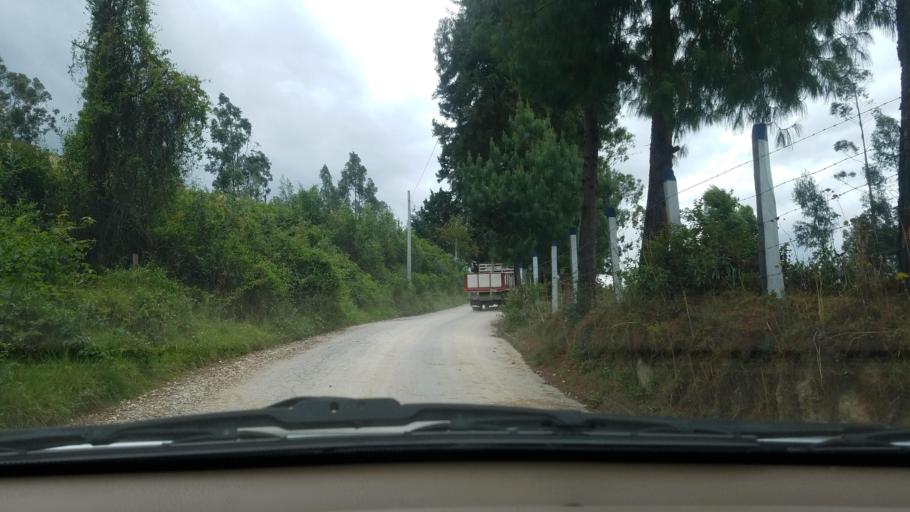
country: CO
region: Boyaca
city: Paipa
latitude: 5.7432
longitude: -73.1102
